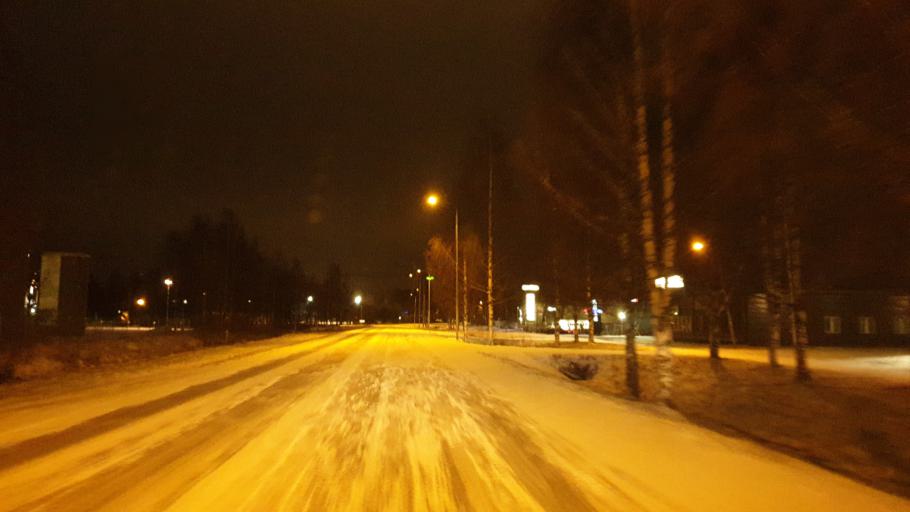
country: FI
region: Northern Ostrobothnia
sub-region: Oulu
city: Oulu
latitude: 64.9958
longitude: 25.4524
